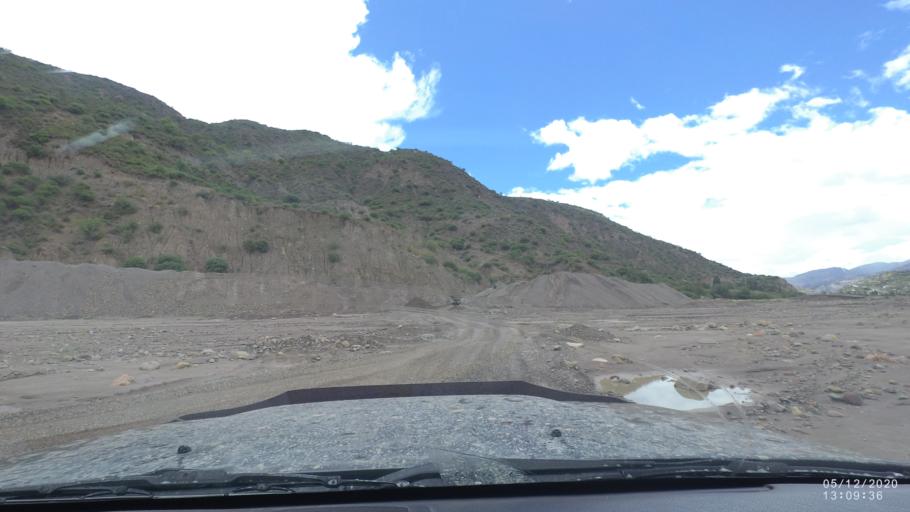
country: BO
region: Cochabamba
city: Sipe Sipe
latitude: -17.5627
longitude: -66.4572
